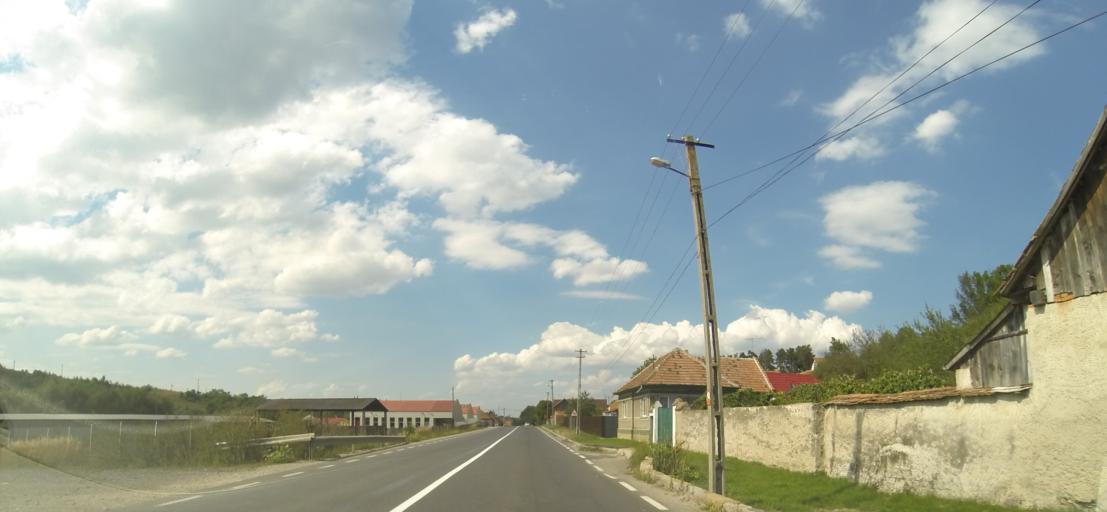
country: RO
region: Brasov
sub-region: Comuna Sinca Veche
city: Persani
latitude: 45.7779
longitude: 25.2169
